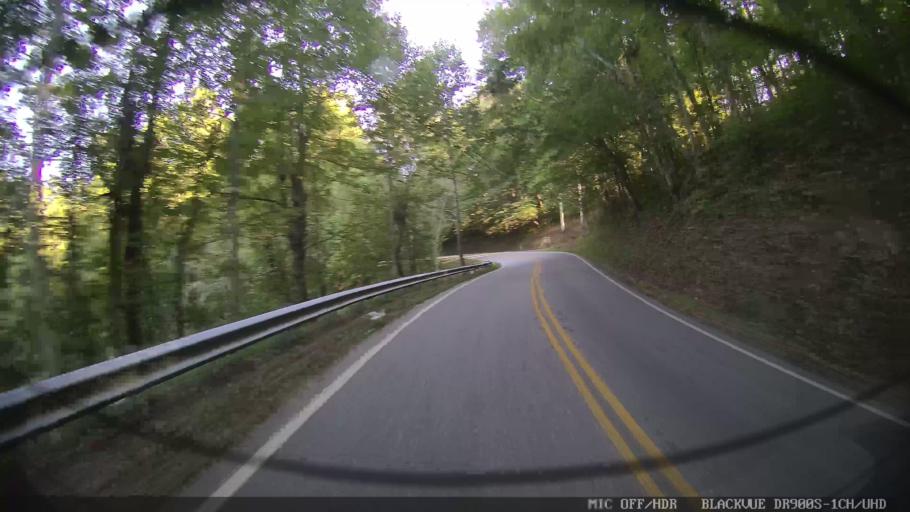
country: US
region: Georgia
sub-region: Lumpkin County
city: Dahlonega
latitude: 34.7031
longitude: -84.0514
